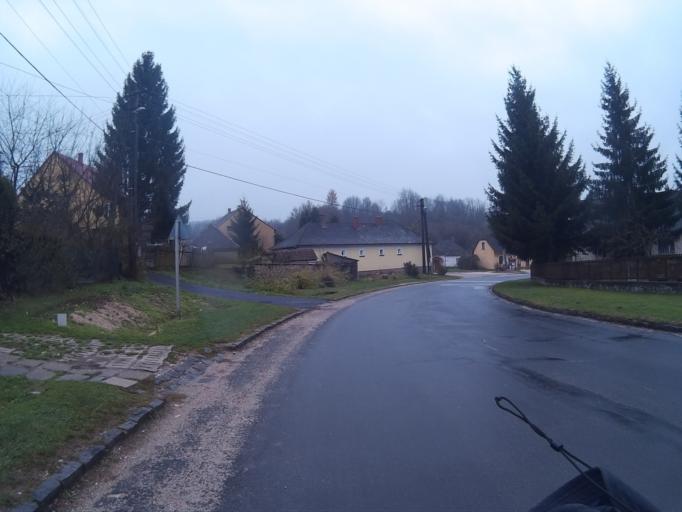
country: HU
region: Veszprem
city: Herend
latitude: 47.2537
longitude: 17.7319
